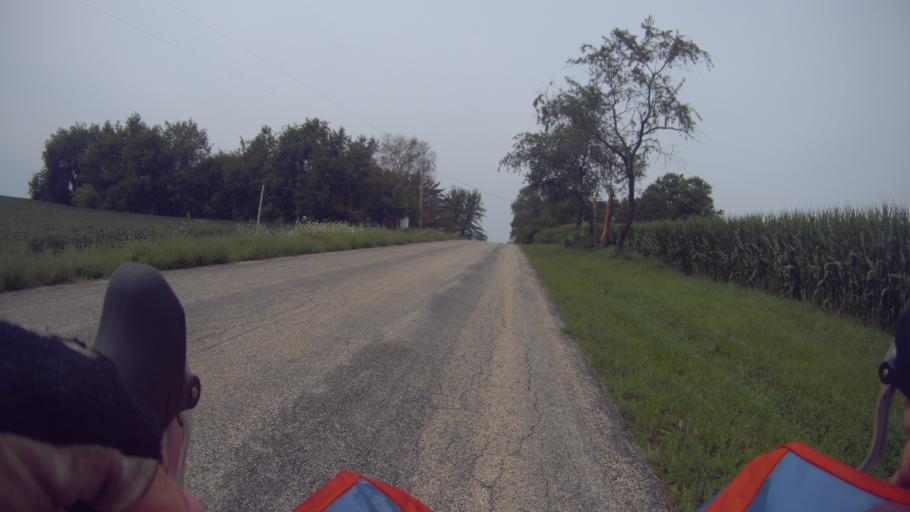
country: US
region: Wisconsin
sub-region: Dane County
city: Mount Horeb
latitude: 42.9846
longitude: -89.6647
